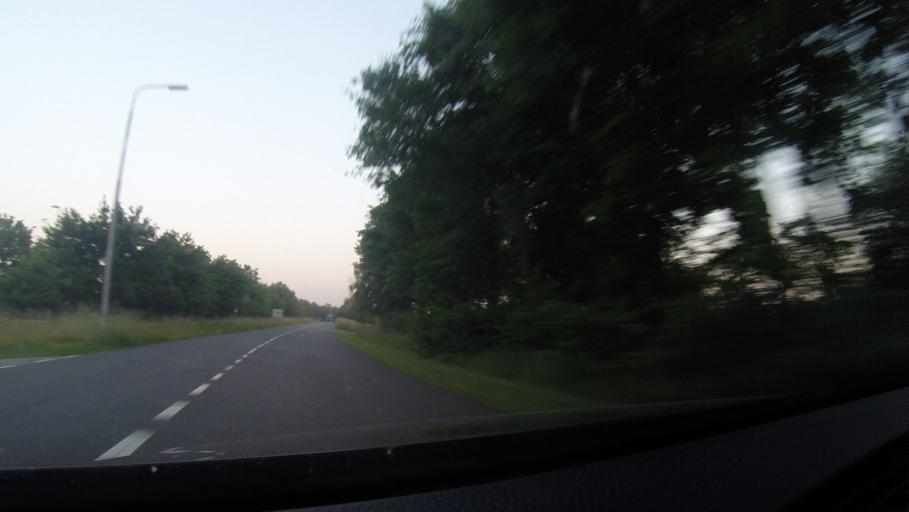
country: NL
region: Gelderland
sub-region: Gemeente Lochem
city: Harfsen
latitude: 52.2440
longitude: 6.3123
